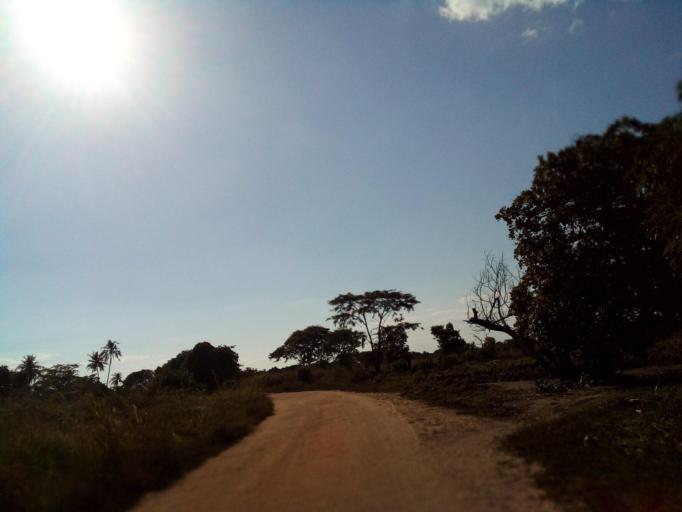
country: MZ
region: Zambezia
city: Quelimane
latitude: -17.5303
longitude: 36.6193
